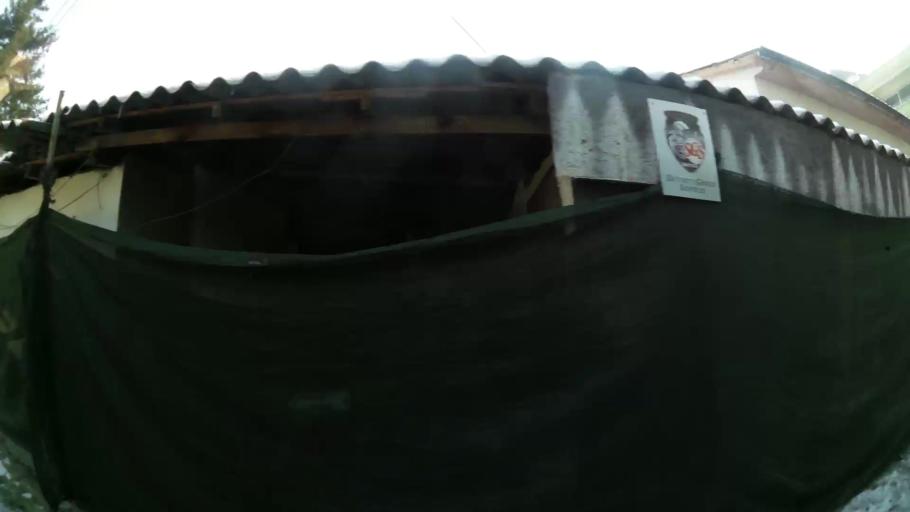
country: MK
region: Karpos
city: Skopje
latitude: 41.9849
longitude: 21.4254
